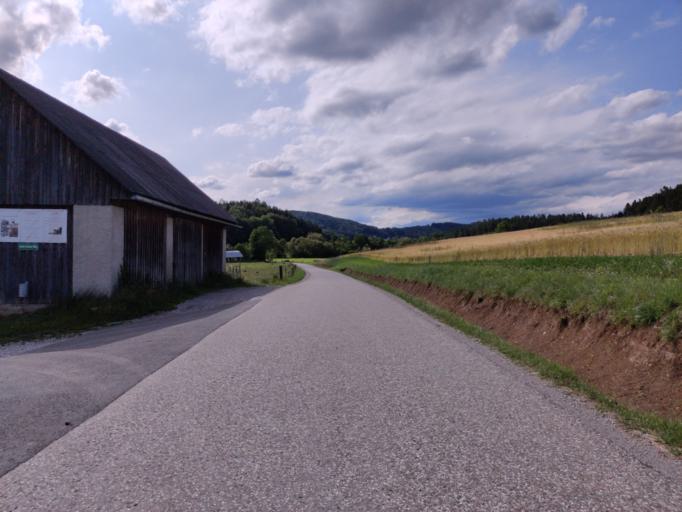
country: AT
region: Styria
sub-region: Politischer Bezirk Graz-Umgebung
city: Thal
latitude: 47.0602
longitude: 15.3502
